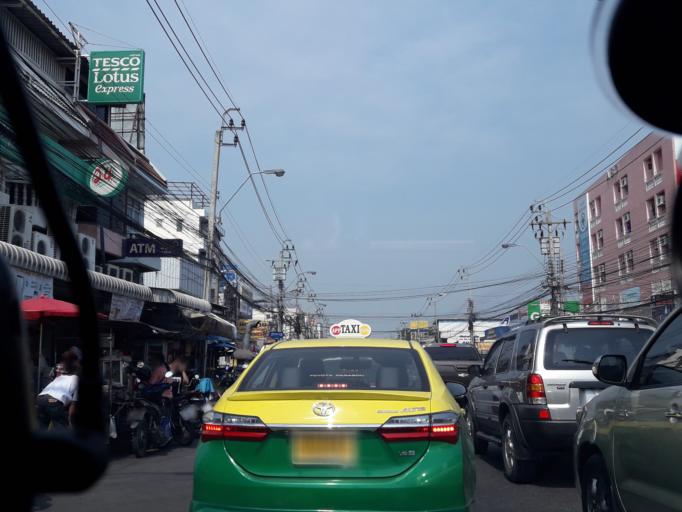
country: TH
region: Bangkok
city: Min Buri
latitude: 13.8236
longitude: 100.7205
